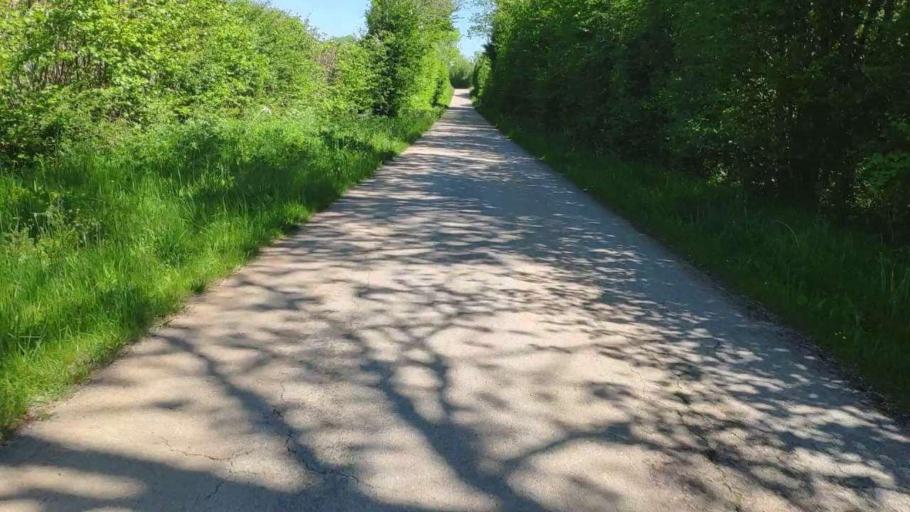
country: FR
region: Franche-Comte
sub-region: Departement du Jura
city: Poligny
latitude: 46.7406
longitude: 5.7401
